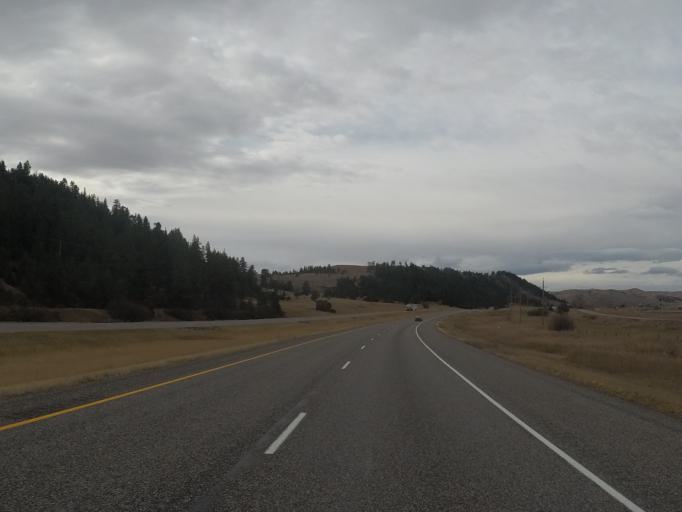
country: US
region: Montana
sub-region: Stillwater County
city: Absarokee
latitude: 45.7076
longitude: -109.5968
